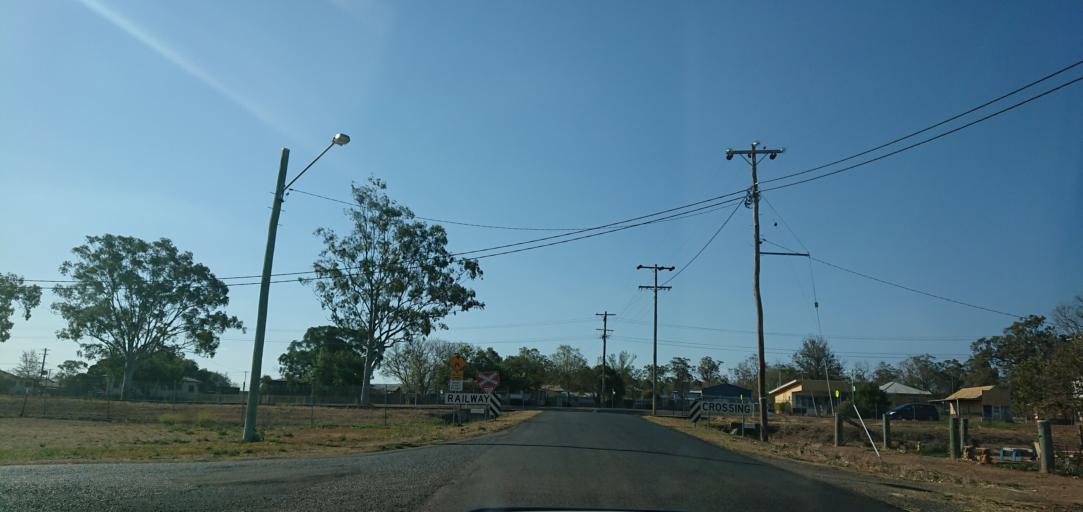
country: AU
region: Queensland
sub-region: Toowoomba
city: Westbrook
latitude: -27.6791
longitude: 151.7129
